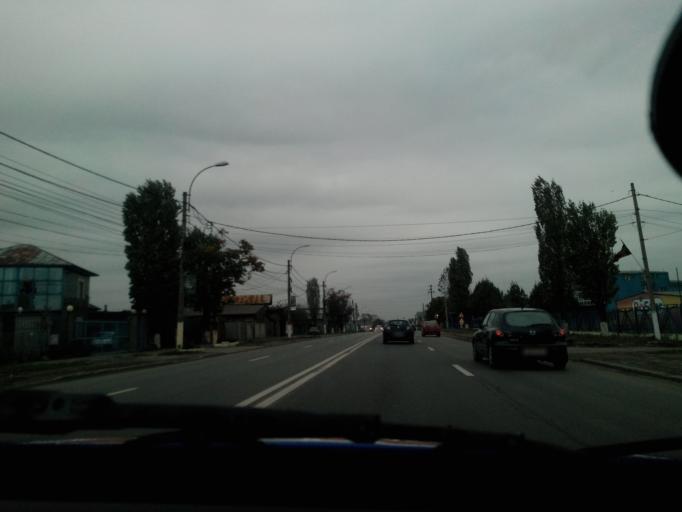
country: RO
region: Ilfov
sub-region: Comuna Magurele
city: Magurele
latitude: 44.3912
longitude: 26.0213
